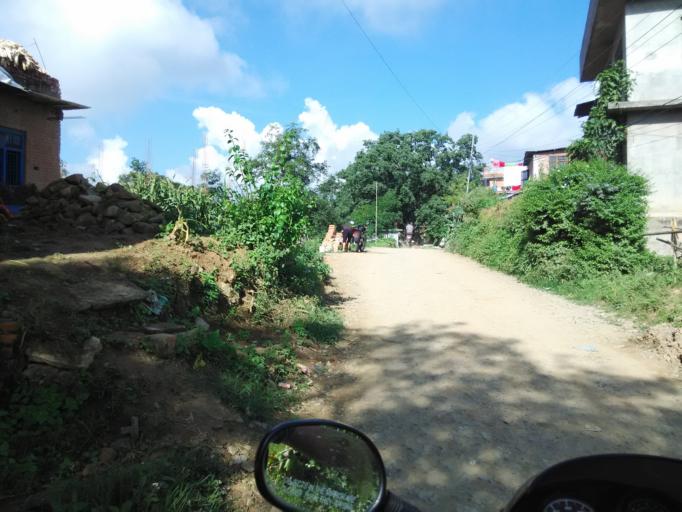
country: NP
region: Central Region
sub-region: Bagmati Zone
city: Patan
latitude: 27.6070
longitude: 85.3427
